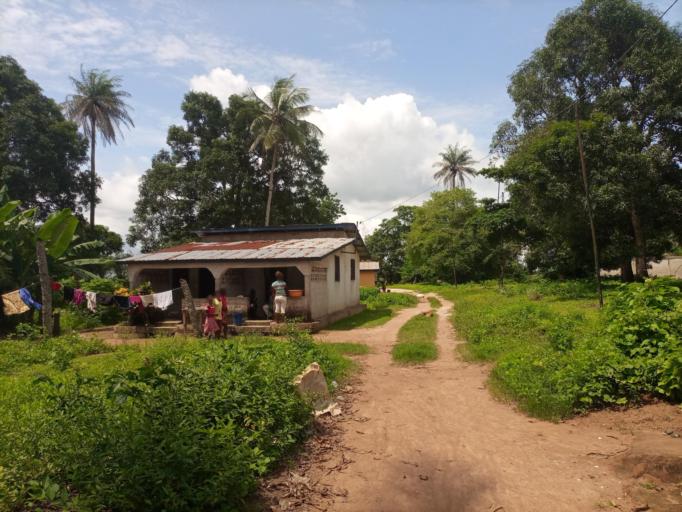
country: SL
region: Northern Province
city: Masoyila
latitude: 8.5394
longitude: -13.1497
